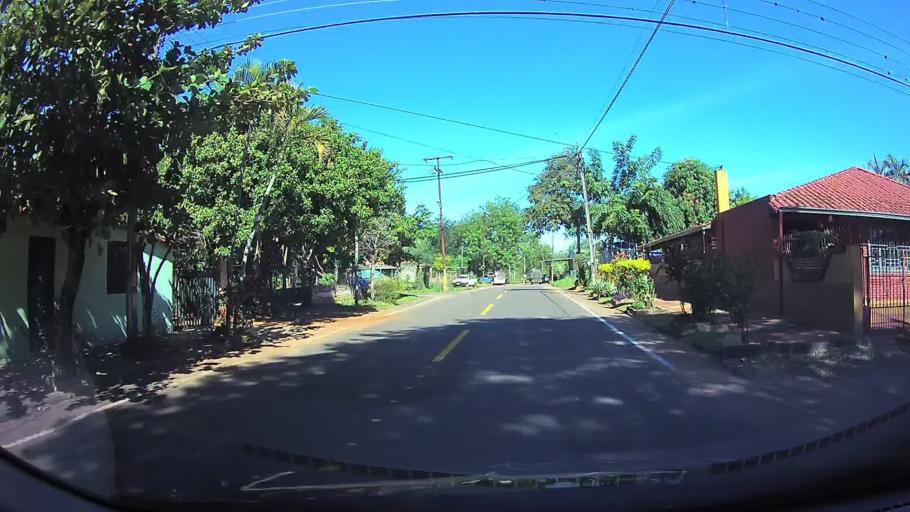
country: PY
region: Central
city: San Lorenzo
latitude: -25.2692
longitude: -57.4722
